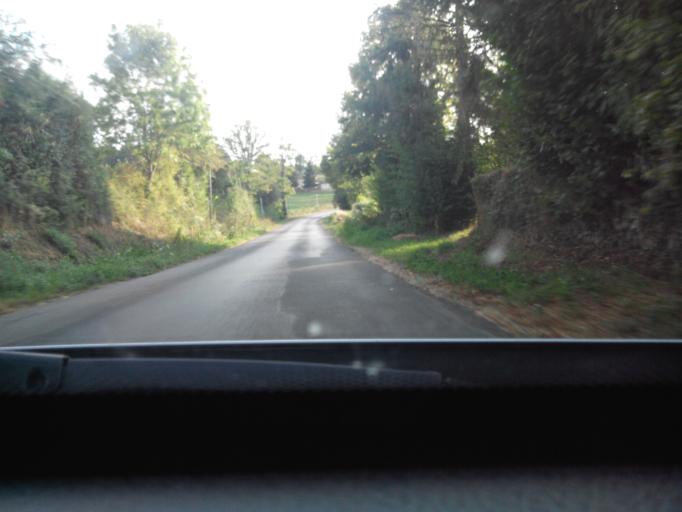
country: FR
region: Poitou-Charentes
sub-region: Departement de la Charente
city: Etagnac
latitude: 45.9225
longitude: 0.7532
